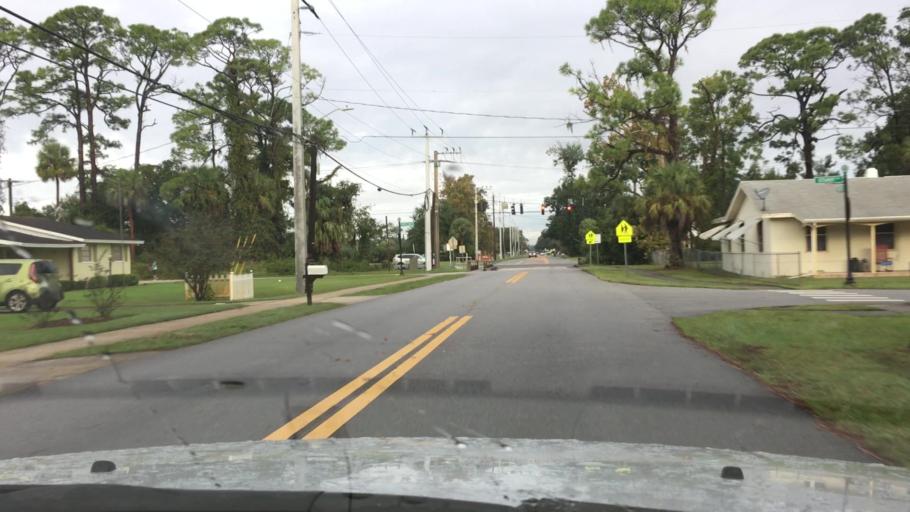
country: US
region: Florida
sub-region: Volusia County
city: Holly Hill
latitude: 29.2415
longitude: -81.0498
